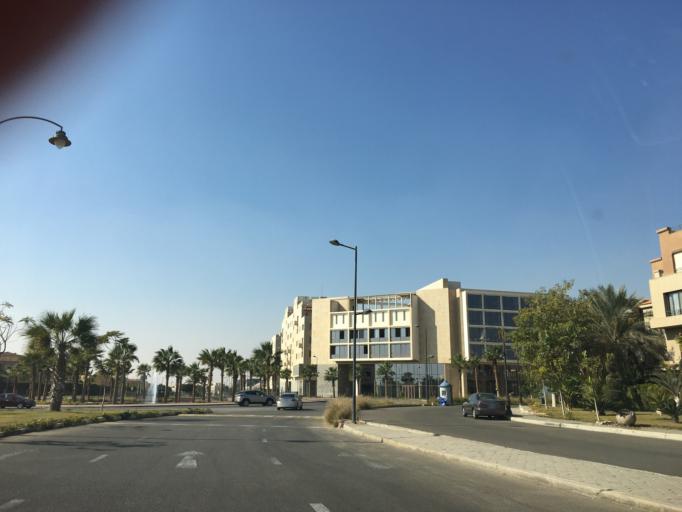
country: EG
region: Al Jizah
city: Awsim
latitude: 30.0654
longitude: 30.9476
